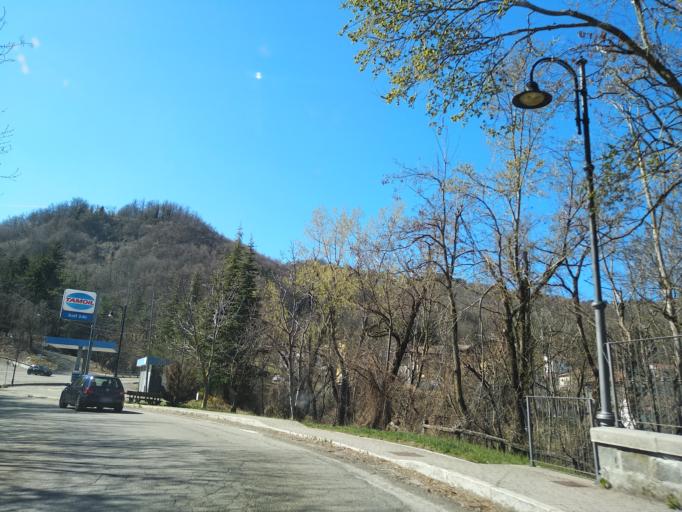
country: IT
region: Emilia-Romagna
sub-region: Provincia di Reggio Emilia
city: Ramiseto
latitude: 44.4124
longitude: 10.2770
